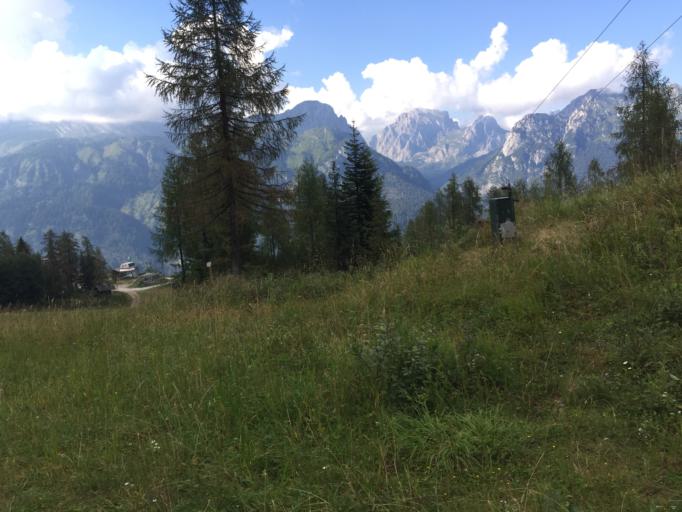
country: IT
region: Veneto
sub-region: Provincia di Belluno
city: Granvilla
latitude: 46.5540
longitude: 12.7215
